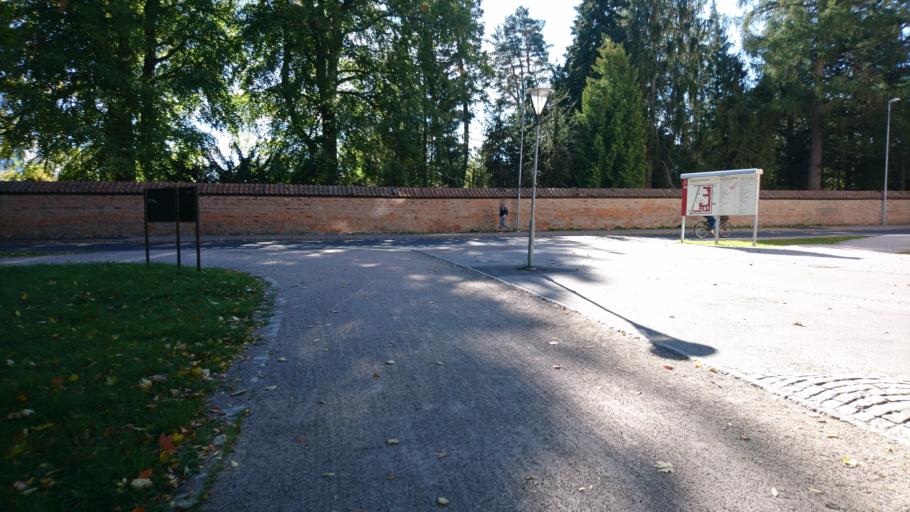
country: SE
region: Uppsala
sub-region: Uppsala Kommun
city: Uppsala
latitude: 59.8536
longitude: 17.6290
